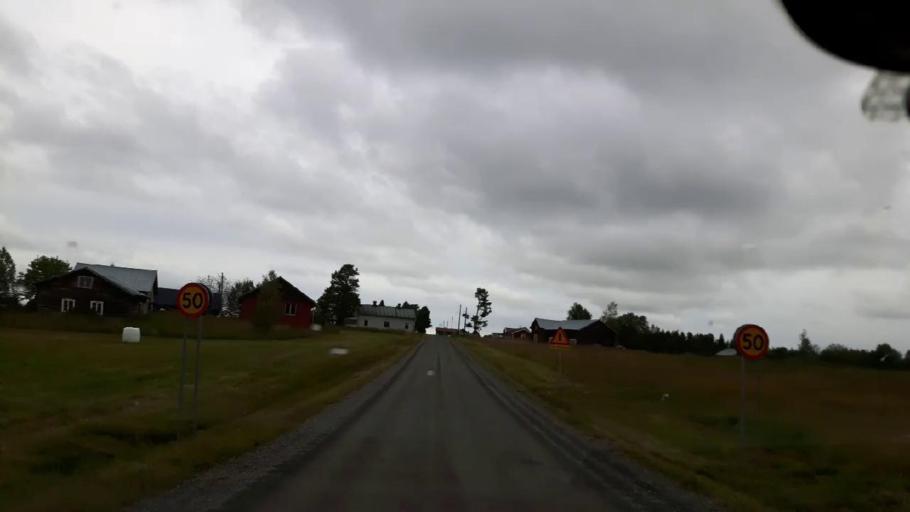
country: SE
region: Jaemtland
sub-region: OEstersunds Kommun
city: Ostersund
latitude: 63.0514
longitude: 14.5681
